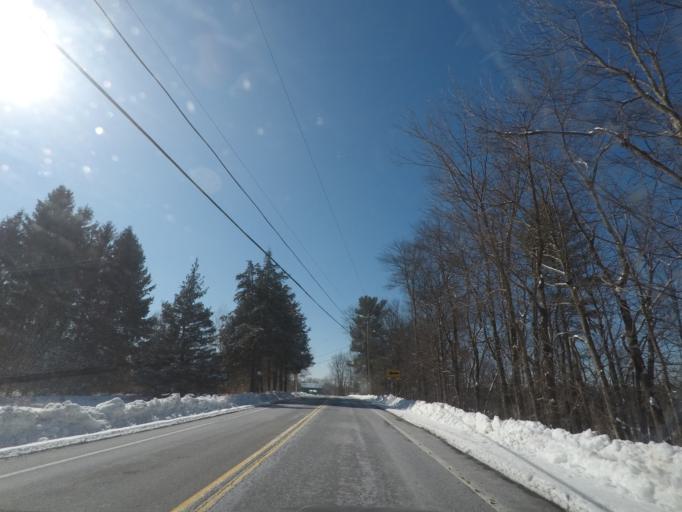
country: US
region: New York
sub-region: Saratoga County
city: Ballston Spa
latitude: 42.9874
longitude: -73.8319
